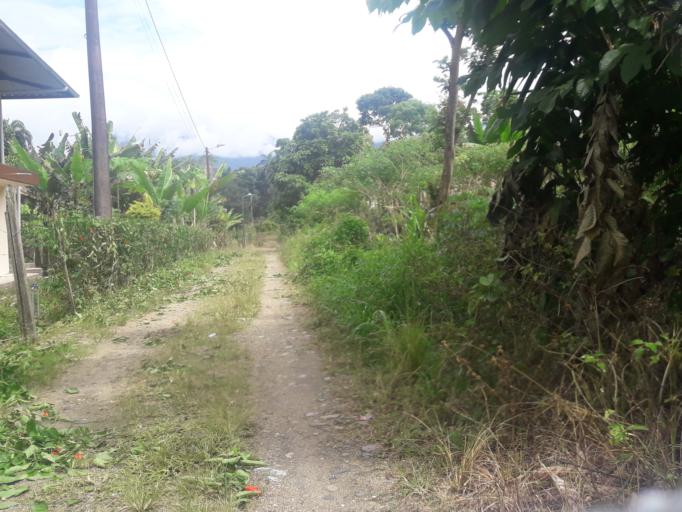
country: EC
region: Napo
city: Tena
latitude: -0.9783
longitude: -77.8471
